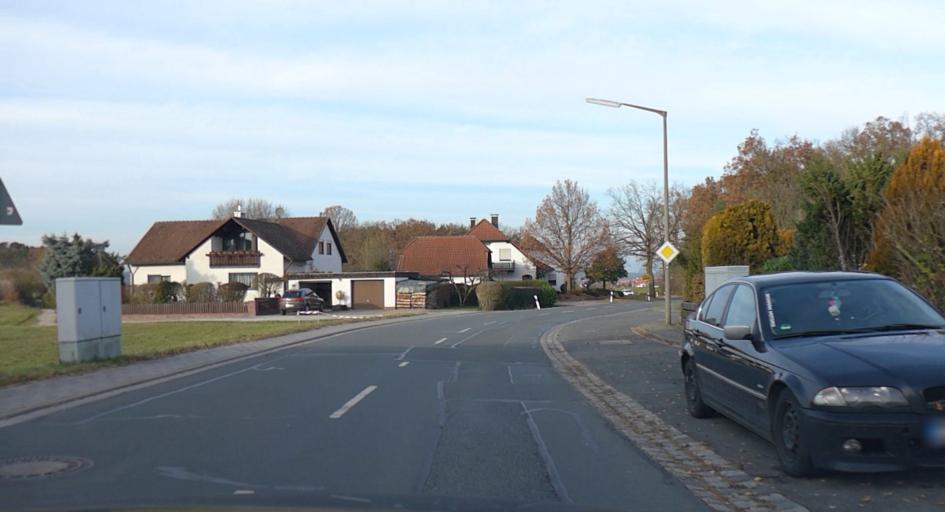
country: DE
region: Bavaria
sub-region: Regierungsbezirk Mittelfranken
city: Bubenreuth
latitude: 49.6343
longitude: 11.0386
